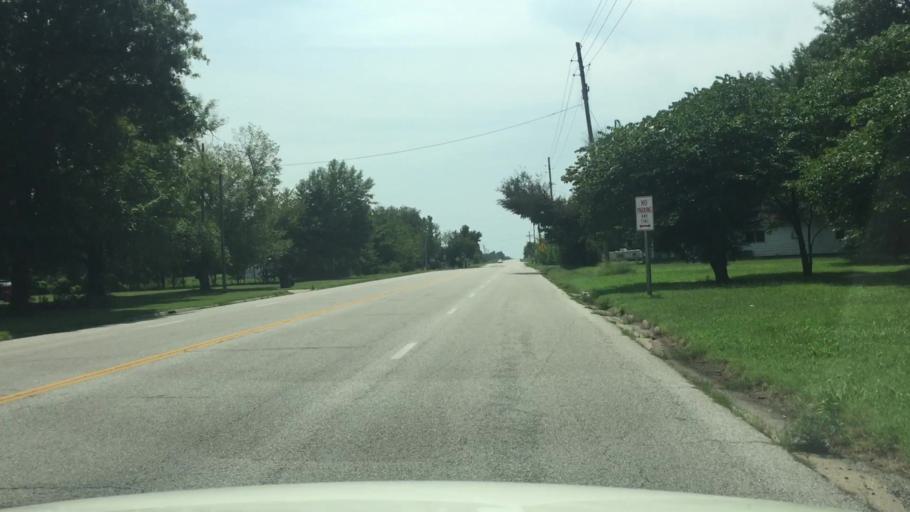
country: US
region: Kansas
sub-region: Cherokee County
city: Galena
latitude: 37.1665
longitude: -94.7044
